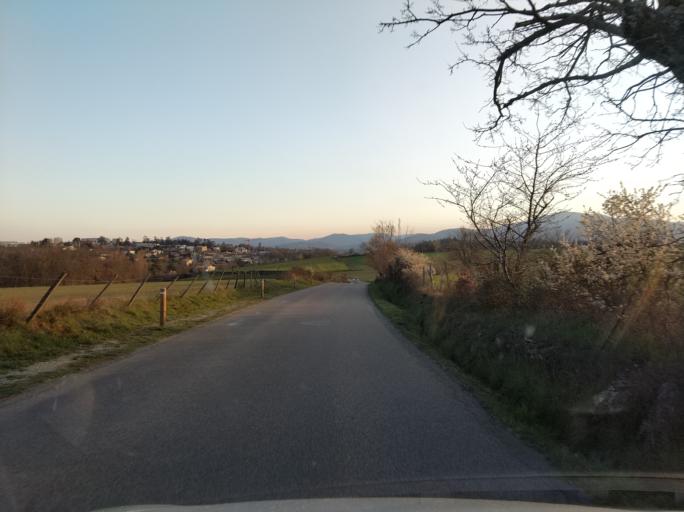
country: FR
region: Rhone-Alpes
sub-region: Departement de l'Ardeche
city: Boulieu-les-Annonay
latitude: 45.2661
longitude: 4.6864
